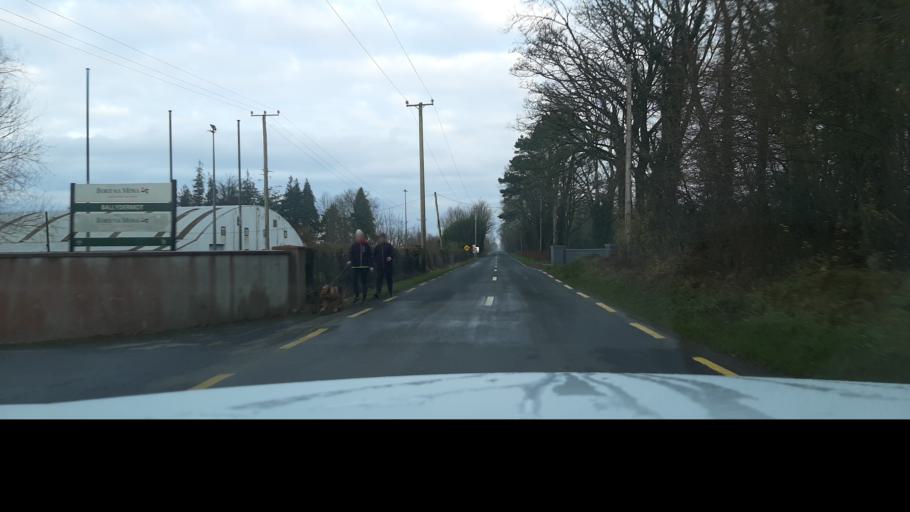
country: IE
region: Leinster
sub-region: Kildare
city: Rathangan
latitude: 53.2403
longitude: -7.0108
